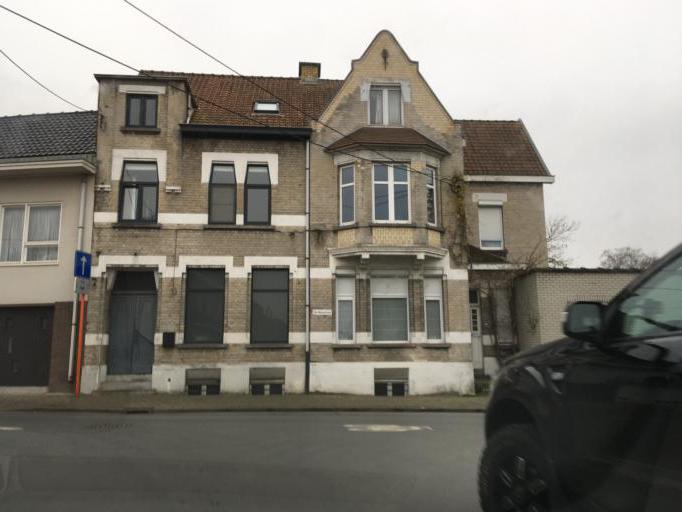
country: BE
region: Flanders
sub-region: Provincie West-Vlaanderen
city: Roeselare
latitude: 50.9345
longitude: 3.1520
